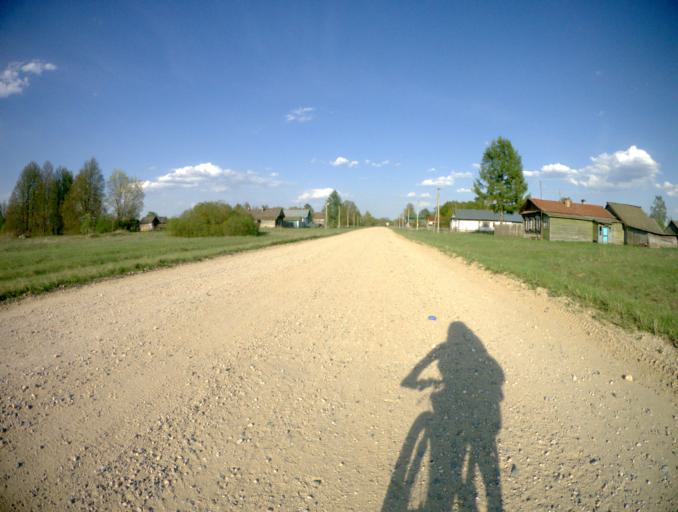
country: RU
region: Ivanovo
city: Kolobovo
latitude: 56.5396
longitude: 41.6274
